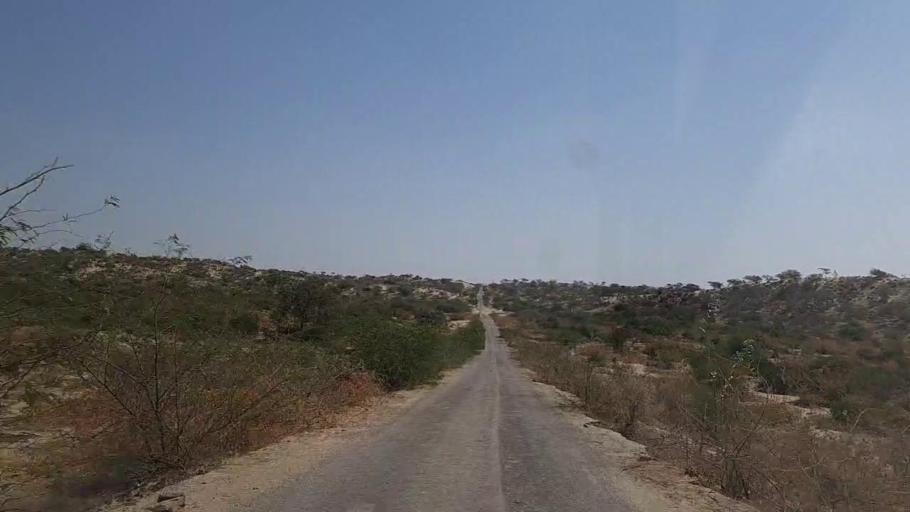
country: PK
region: Sindh
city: Diplo
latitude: 24.4897
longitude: 69.4400
